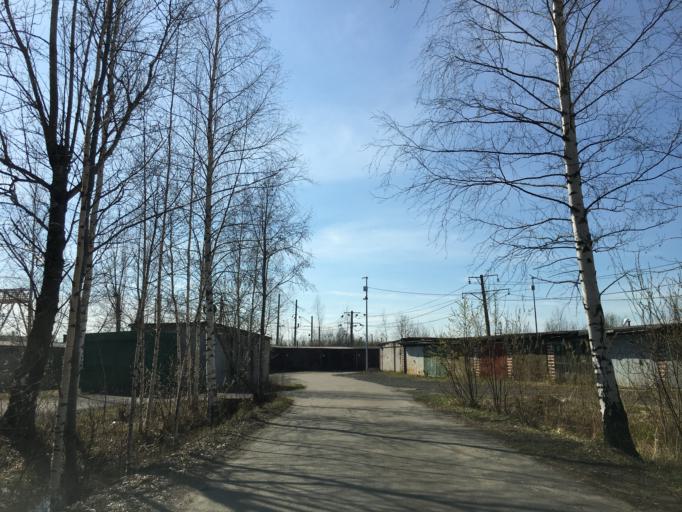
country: RU
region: St.-Petersburg
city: Uritsk
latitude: 59.8194
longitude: 30.1642
